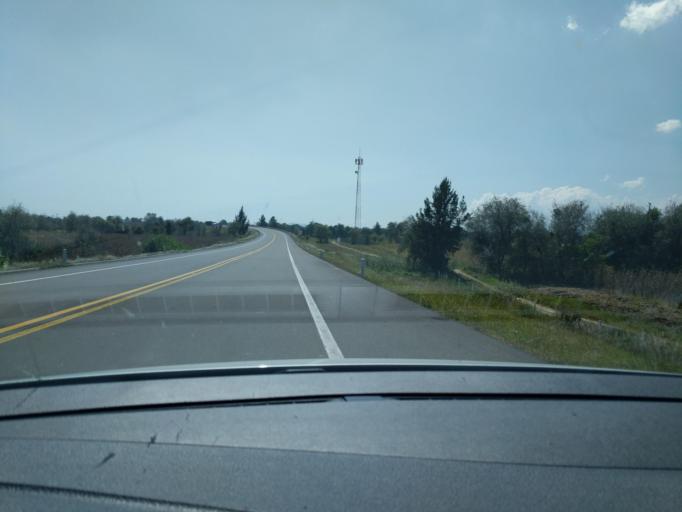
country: MX
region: Tlaxcala
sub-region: Xicohtzinco
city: Santo Toribio Xicohtzingo
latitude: 19.1818
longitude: -98.2704
